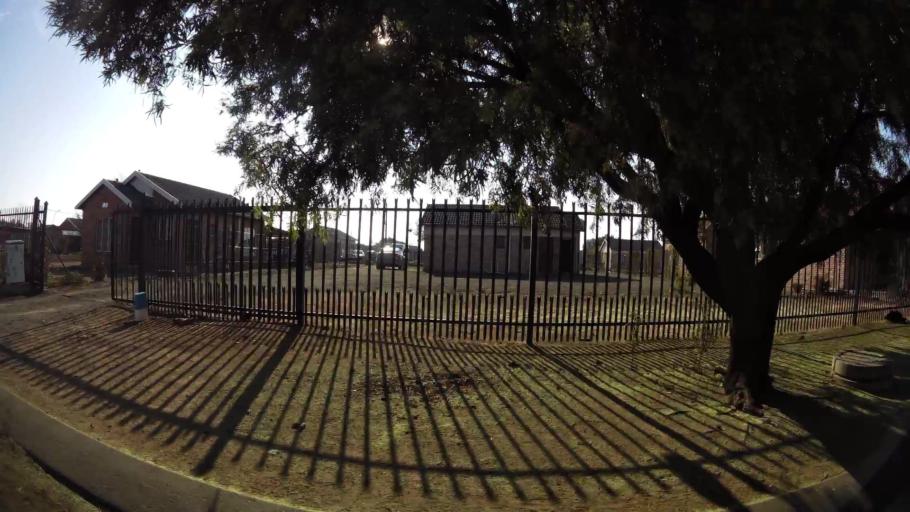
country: ZA
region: Orange Free State
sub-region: Mangaung Metropolitan Municipality
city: Bloemfontein
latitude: -29.1841
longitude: 26.1725
